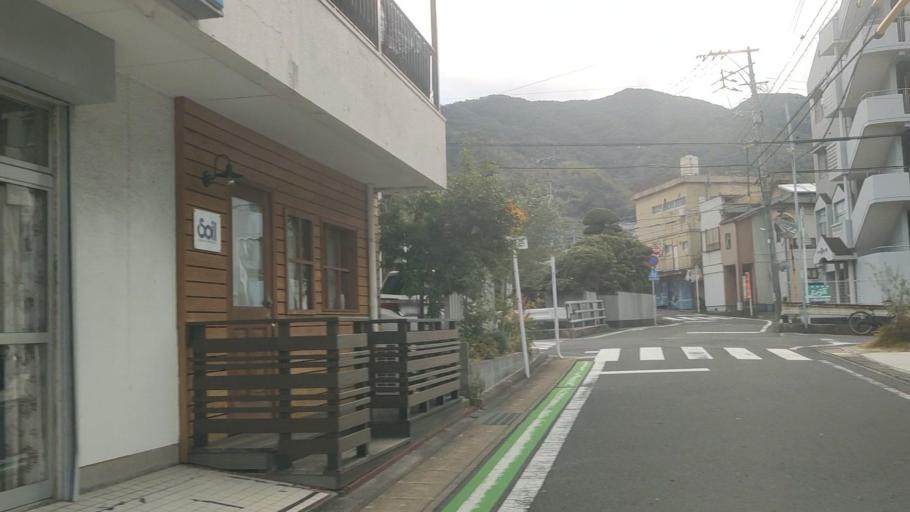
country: JP
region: Nagasaki
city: Nagasaki-shi
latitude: 32.7779
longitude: 129.8700
